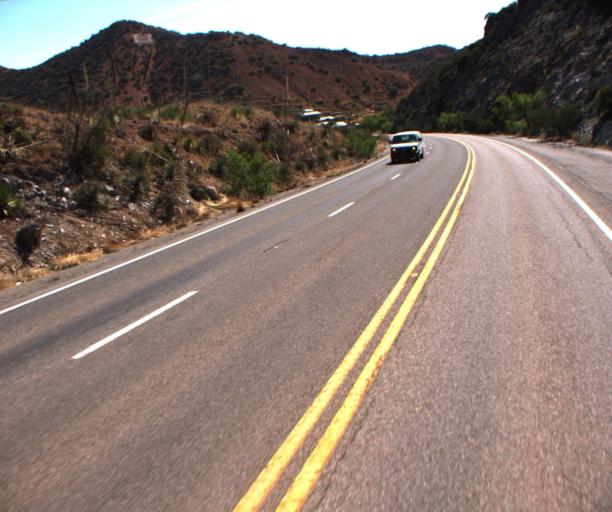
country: US
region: Arizona
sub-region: Cochise County
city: Bisbee
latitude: 31.4406
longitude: -109.9195
